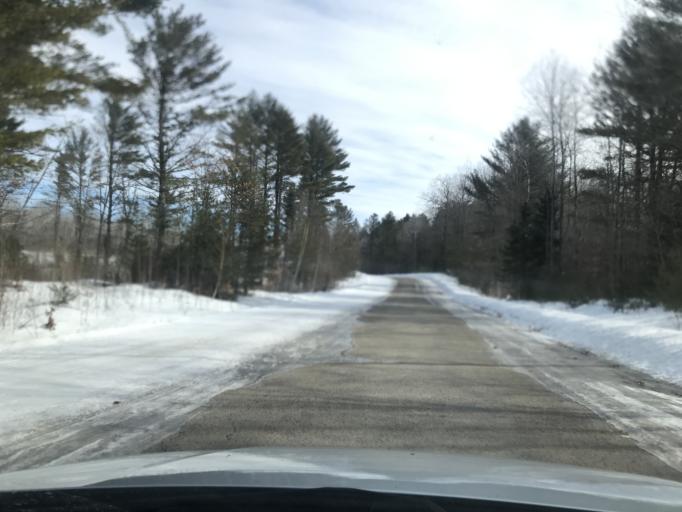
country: US
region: Wisconsin
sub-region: Menominee County
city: Legend Lake
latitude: 45.1093
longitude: -88.4414
